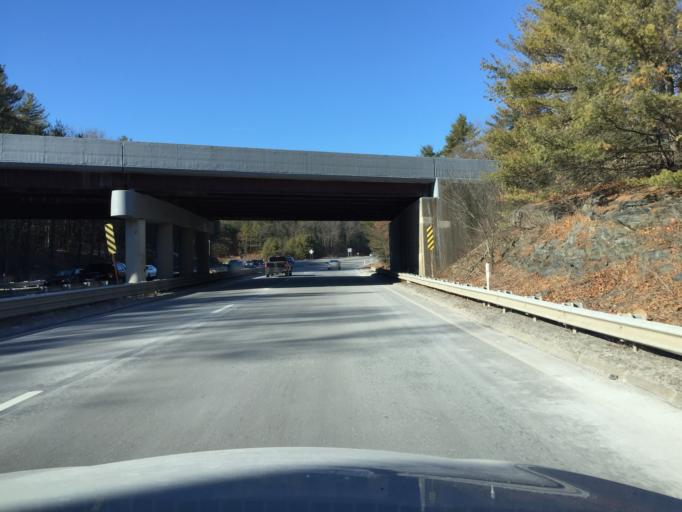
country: US
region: Massachusetts
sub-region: Norfolk County
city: Foxborough
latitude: 42.0431
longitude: -71.2425
